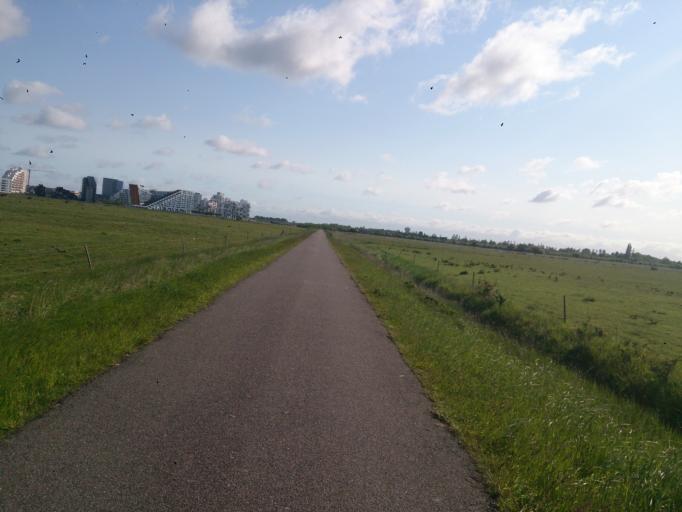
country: DK
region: Capital Region
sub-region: Tarnby Kommune
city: Tarnby
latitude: 55.6089
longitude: 12.5649
